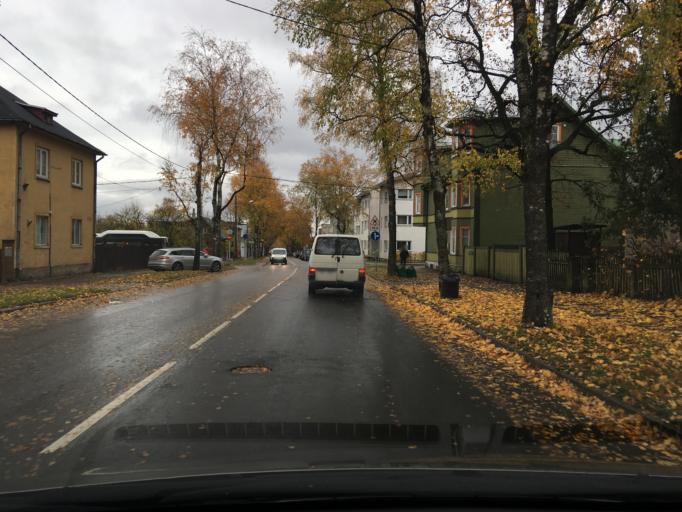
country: EE
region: Tartu
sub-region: Tartu linn
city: Tartu
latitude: 58.3645
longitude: 26.7337
